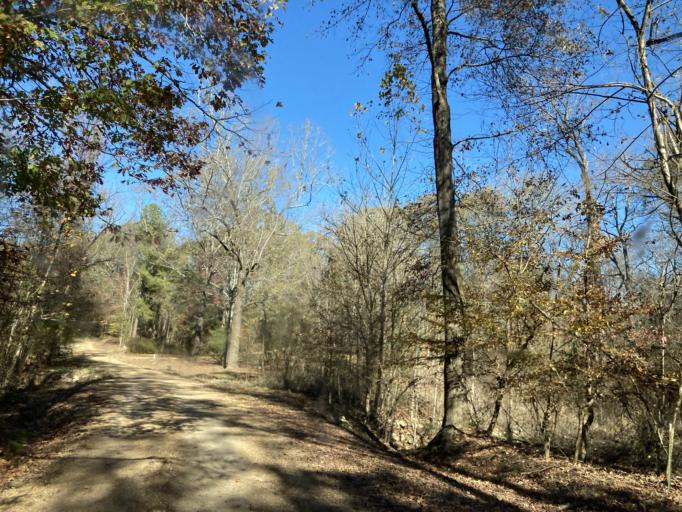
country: US
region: Mississippi
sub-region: Hinds County
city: Lynchburg
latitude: 32.5556
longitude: -90.4998
